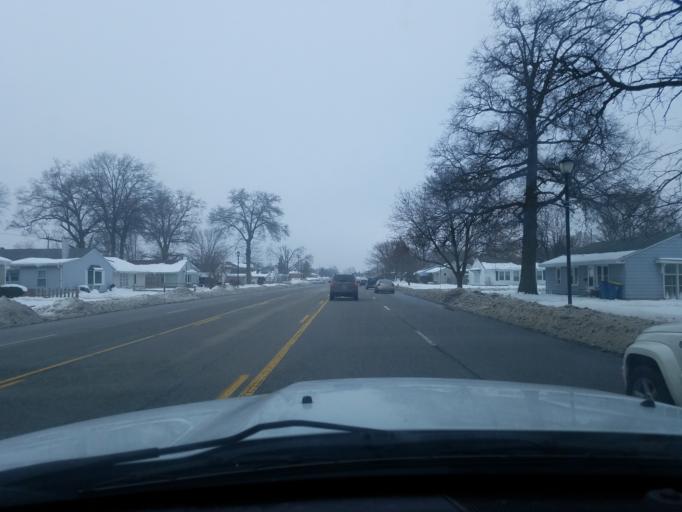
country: US
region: Indiana
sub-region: Saint Joseph County
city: Mishawaka
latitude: 41.6858
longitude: -86.1815
